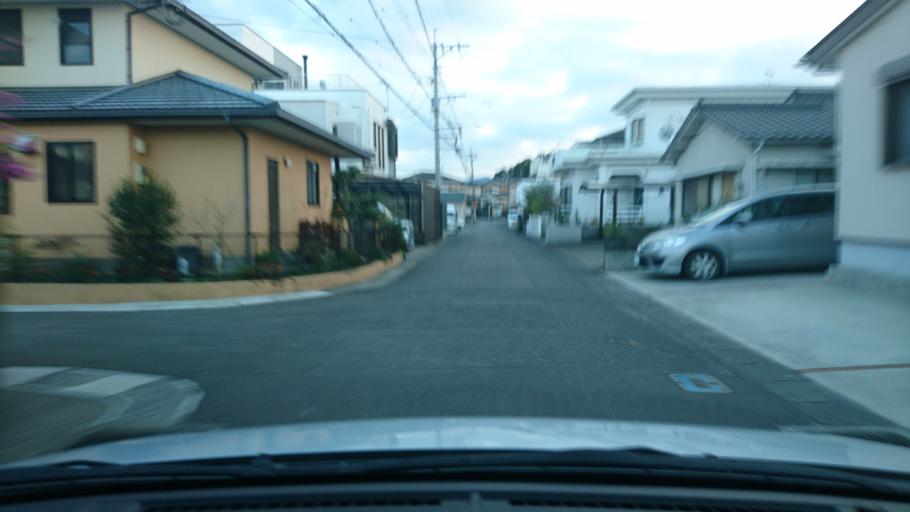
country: JP
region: Miyazaki
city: Miyazaki-shi
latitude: 31.8586
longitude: 131.4240
